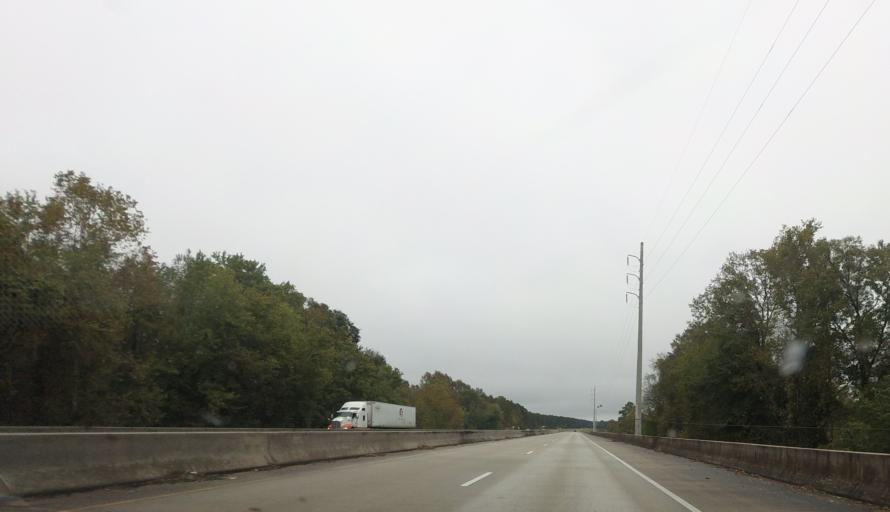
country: US
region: Georgia
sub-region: Taylor County
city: Reynolds
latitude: 32.5427
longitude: -84.0161
